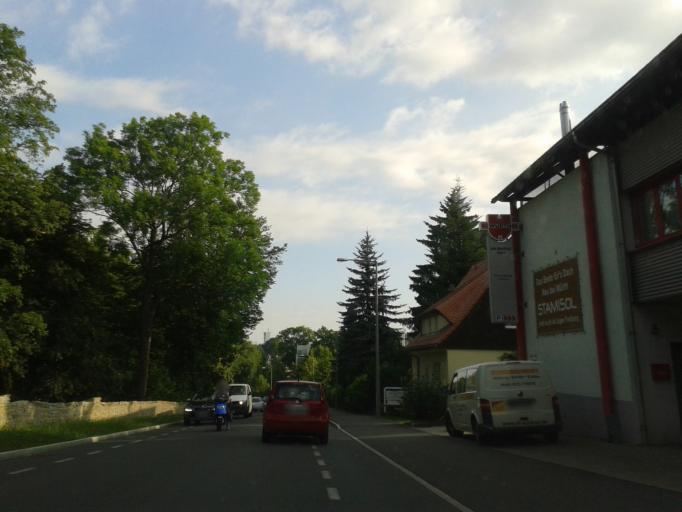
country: DE
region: Saxony
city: Freiberg
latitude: 50.9190
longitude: 13.3503
